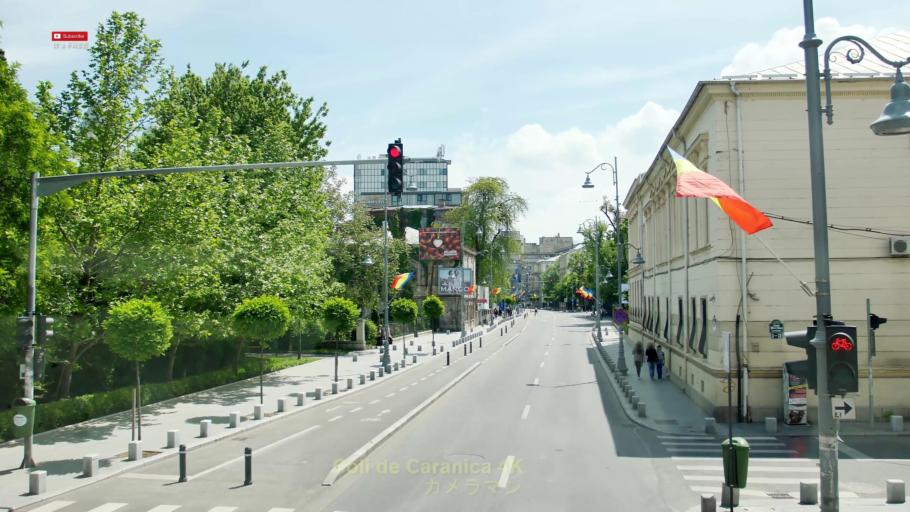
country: RO
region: Bucuresti
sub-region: Municipiul Bucuresti
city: Bucuresti
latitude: 44.4471
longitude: 26.0900
